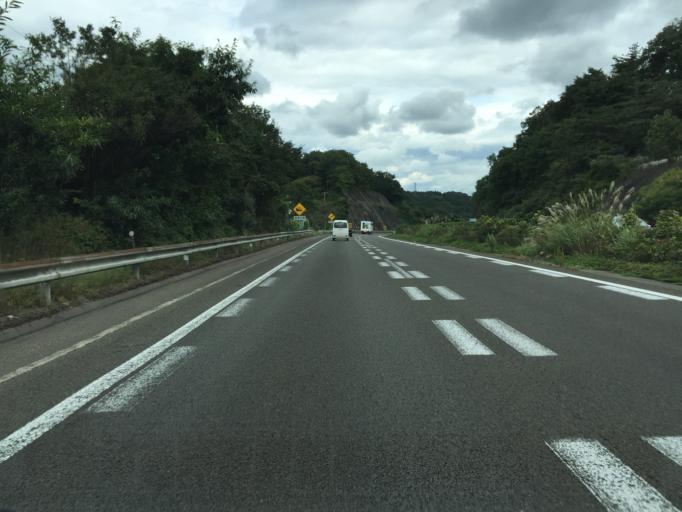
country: JP
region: Miyagi
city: Shiroishi
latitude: 37.9418
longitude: 140.6120
